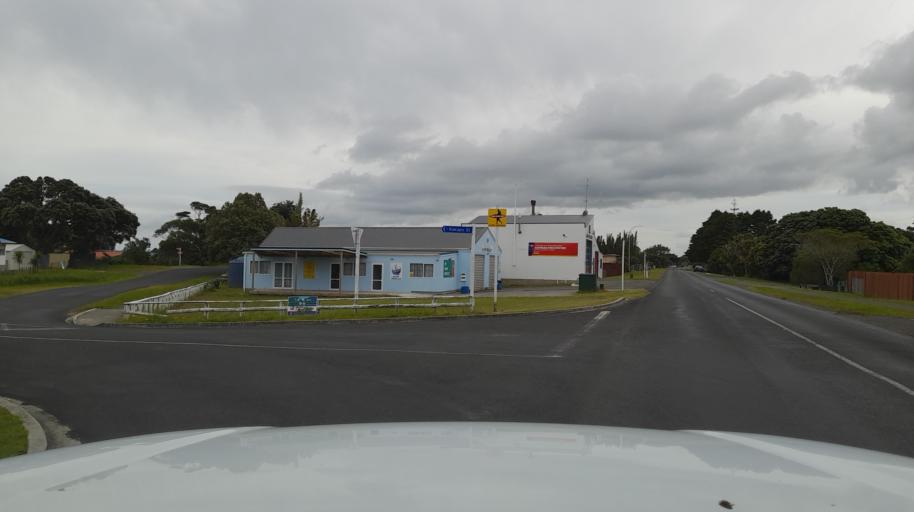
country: NZ
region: Northland
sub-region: Far North District
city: Ahipara
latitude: -35.1671
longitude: 173.1544
